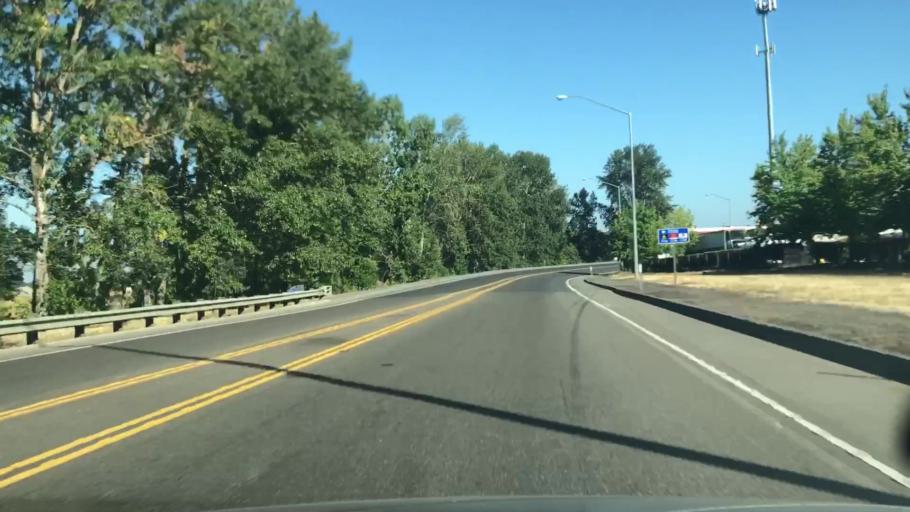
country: US
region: Washington
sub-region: Clark County
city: Vancouver
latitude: 45.5870
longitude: -122.6777
